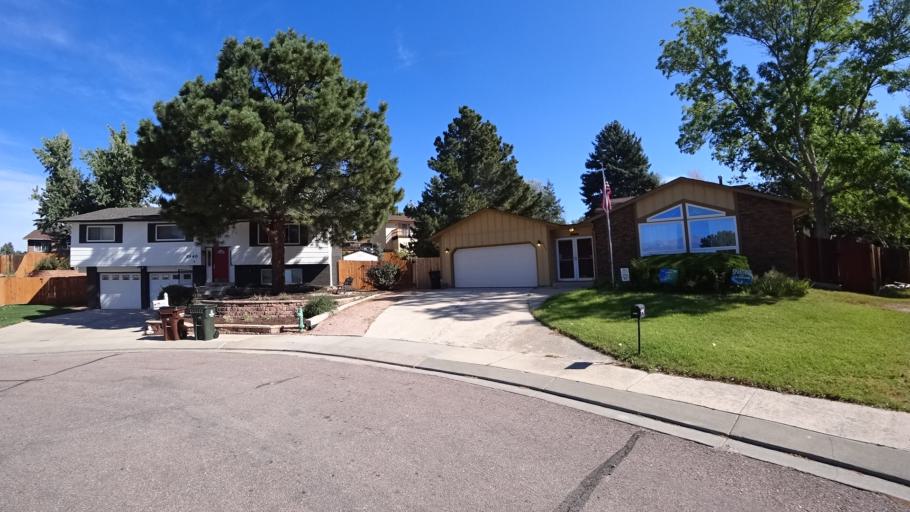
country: US
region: Colorado
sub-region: El Paso County
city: Cimarron Hills
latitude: 38.9163
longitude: -104.7730
